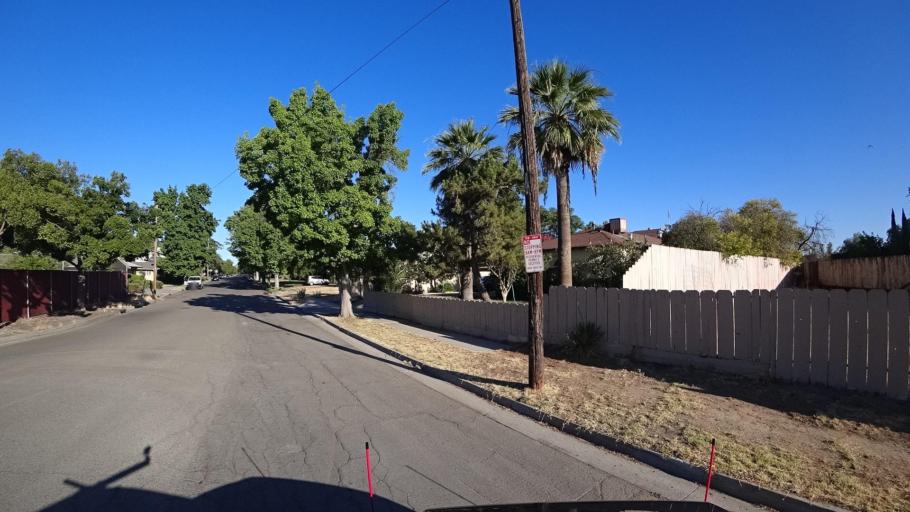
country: US
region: California
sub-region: Fresno County
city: Fresno
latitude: 36.7705
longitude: -119.7959
